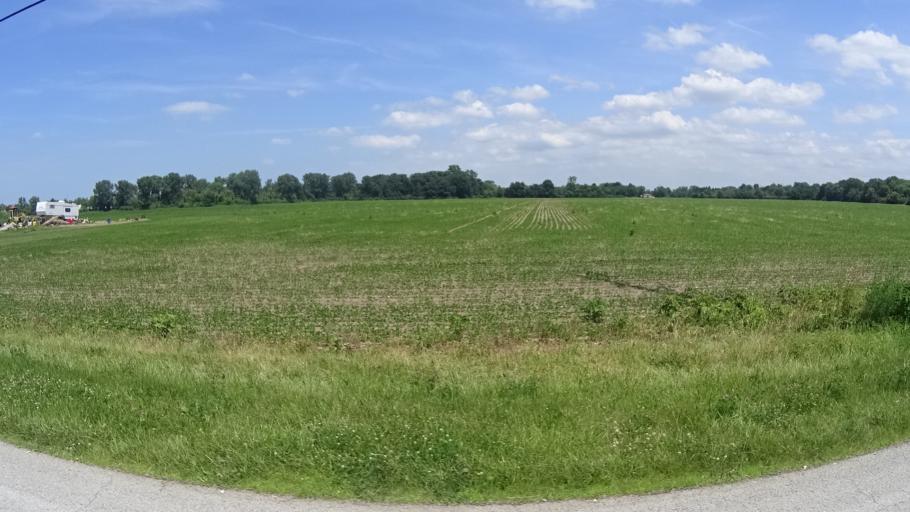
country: US
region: Ohio
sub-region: Erie County
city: Huron
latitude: 41.3827
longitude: -82.5488
